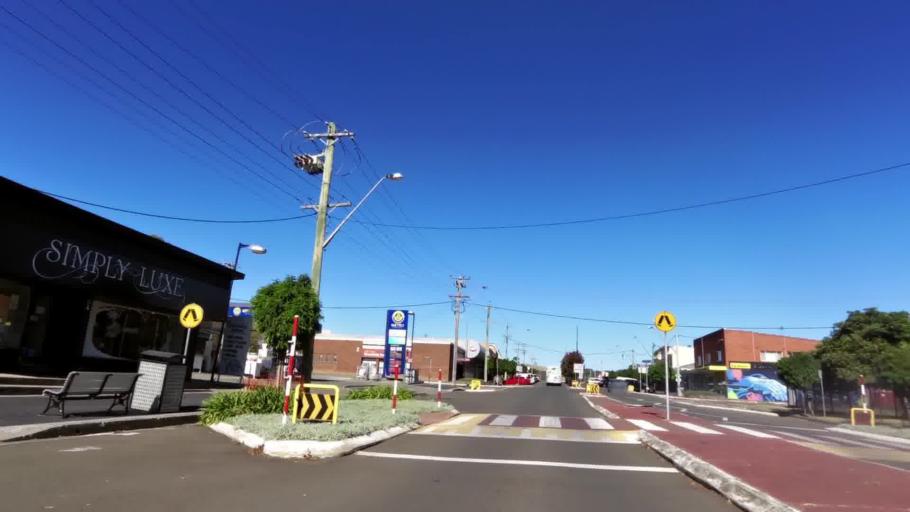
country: AU
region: New South Wales
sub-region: Shellharbour
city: Albion Park Rail
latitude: -34.5624
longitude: 150.8190
